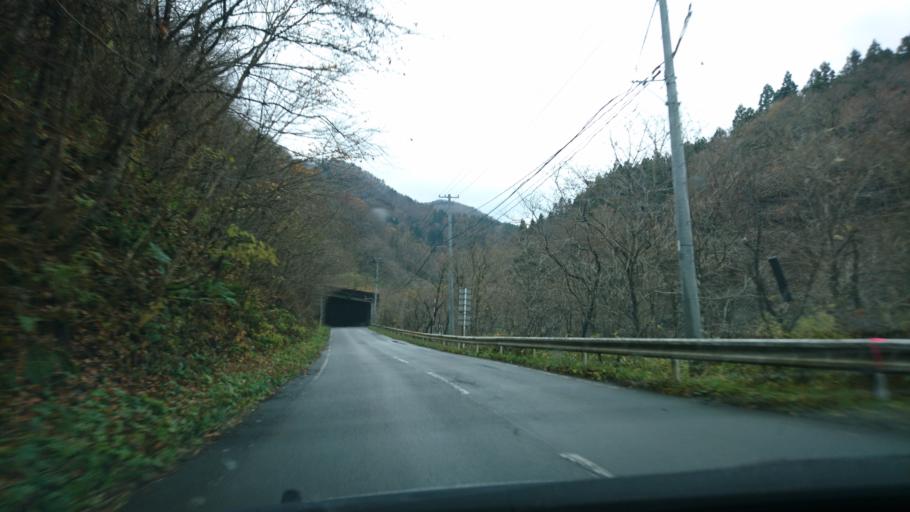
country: JP
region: Iwate
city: Ichinoseki
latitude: 38.9093
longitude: 140.8876
